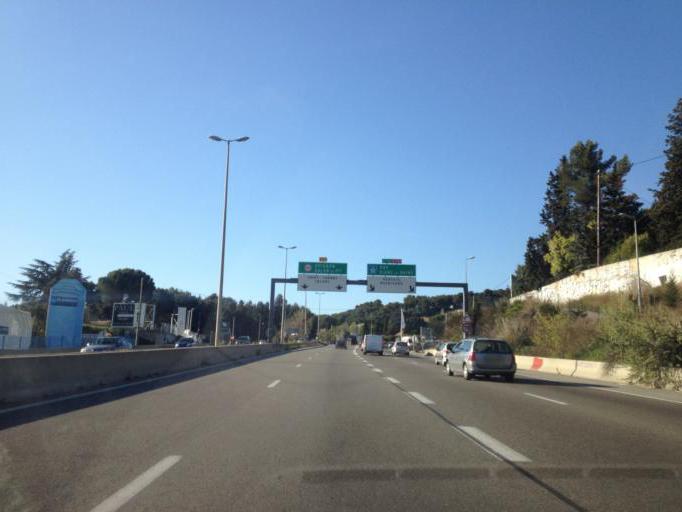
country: FR
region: Provence-Alpes-Cote d'Azur
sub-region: Departement des Bouches-du-Rhone
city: Aix-en-Provence
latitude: 43.5471
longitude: 5.4287
